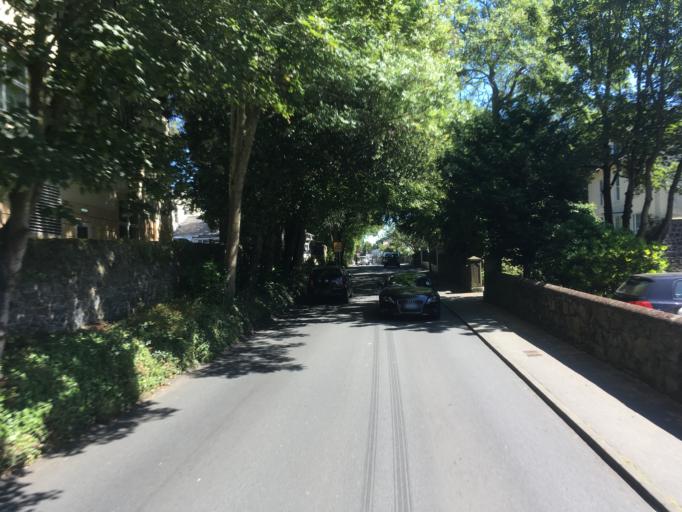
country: GG
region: St Peter Port
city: Saint Peter Port
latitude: 49.4575
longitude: -2.5521
